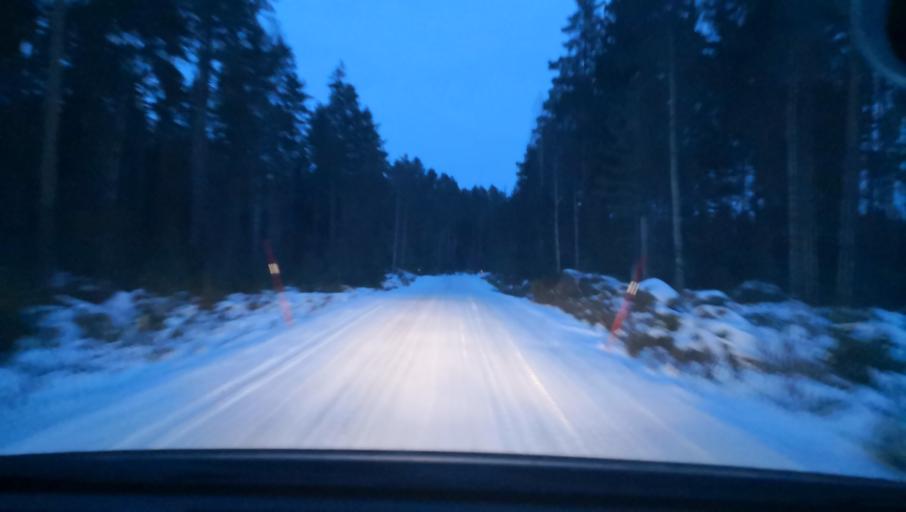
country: SE
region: Dalarna
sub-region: Avesta Kommun
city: Horndal
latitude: 60.2330
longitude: 16.6517
